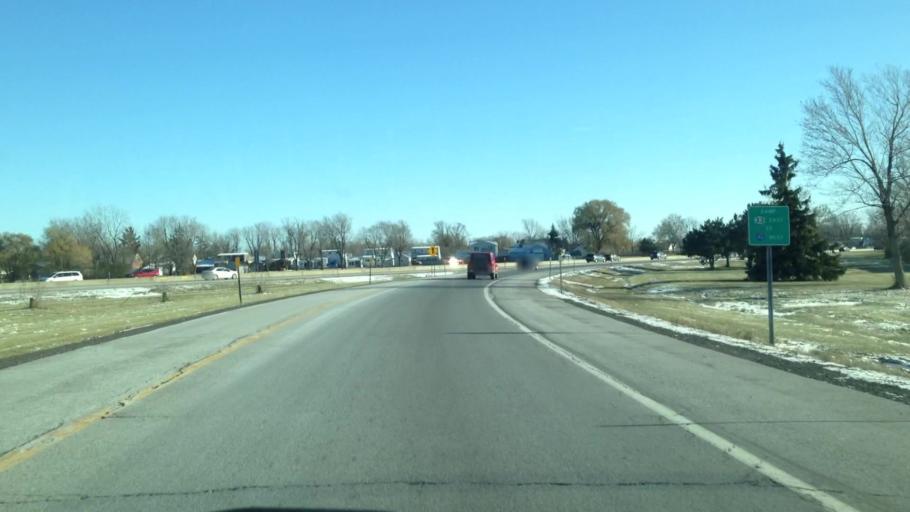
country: US
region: New York
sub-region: Erie County
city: Cheektowaga
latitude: 42.9305
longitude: -78.7676
